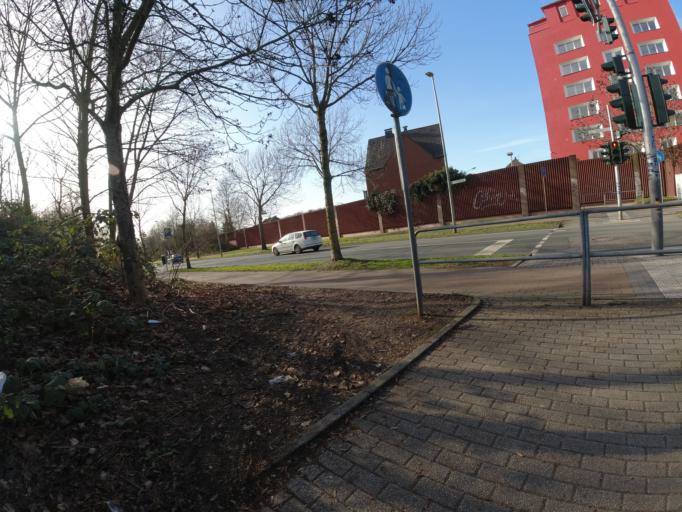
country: DE
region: North Rhine-Westphalia
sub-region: Regierungsbezirk Dusseldorf
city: Hochfeld
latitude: 51.4034
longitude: 6.7009
